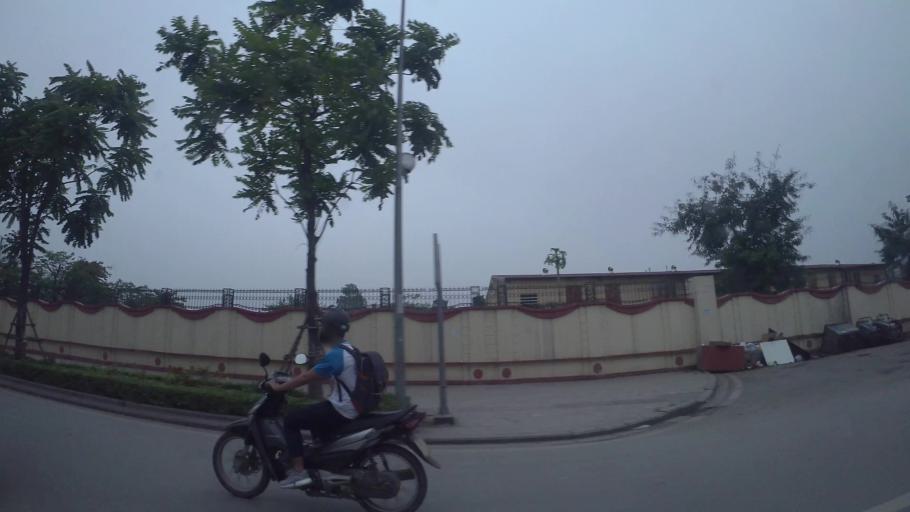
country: VN
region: Ha Noi
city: Hai BaTrung
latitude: 20.9886
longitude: 105.8349
